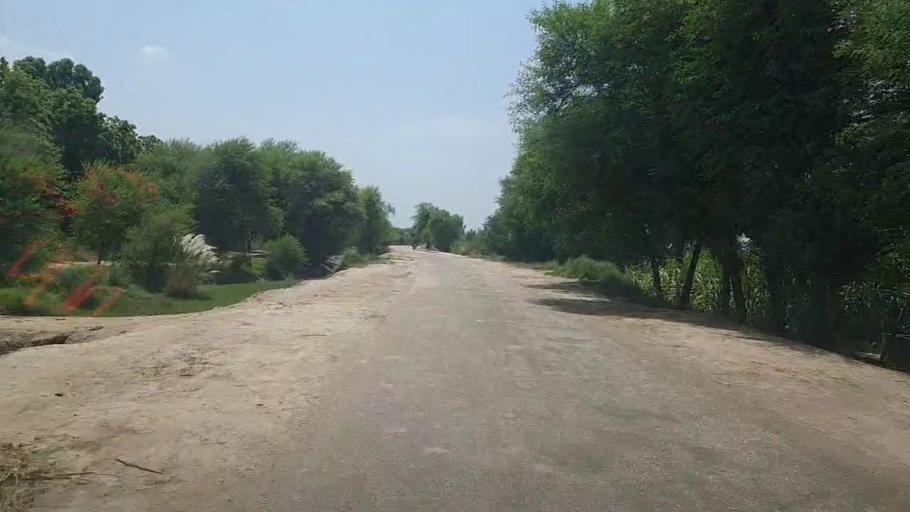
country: PK
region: Sindh
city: Ubauro
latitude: 28.2856
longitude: 69.8089
